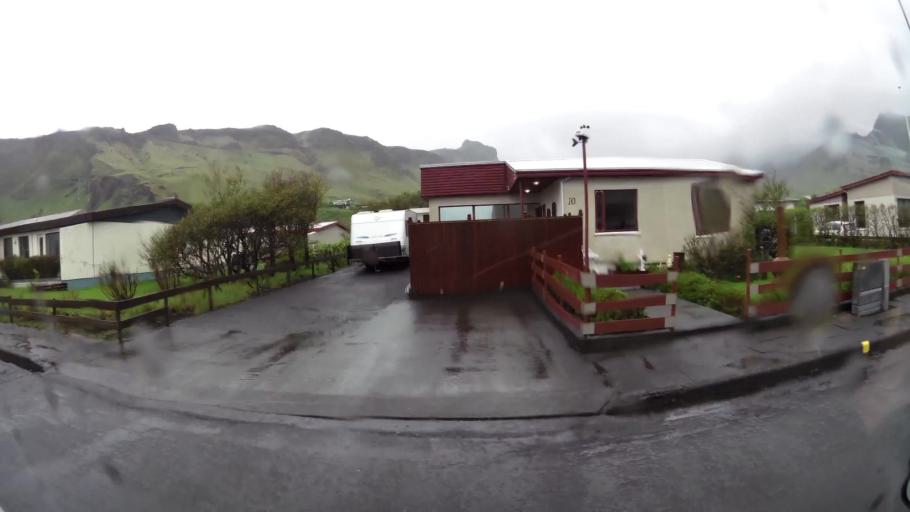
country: IS
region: South
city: Vestmannaeyjar
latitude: 63.4173
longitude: -19.0087
